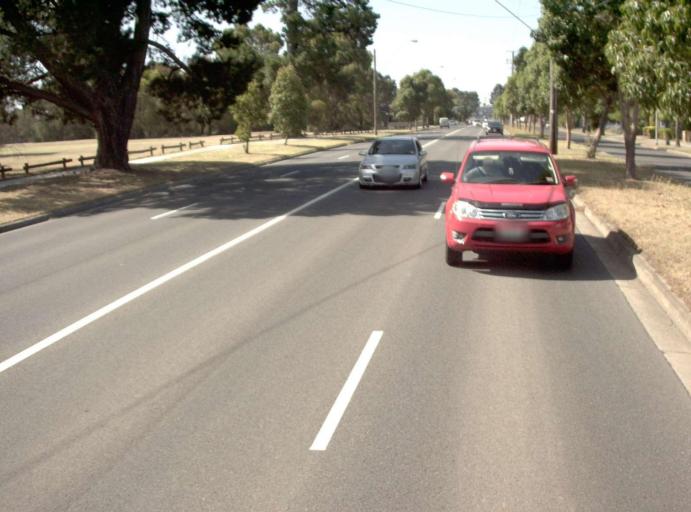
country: AU
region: Victoria
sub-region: Monash
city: Mulgrave
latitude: -37.9158
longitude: 145.1875
